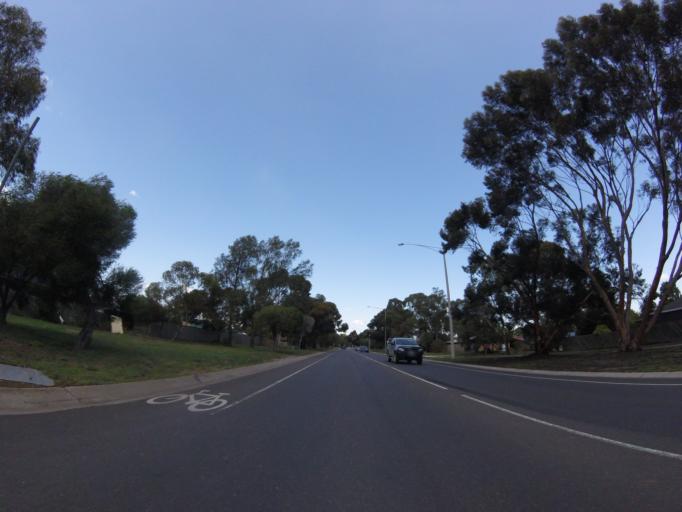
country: AU
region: Victoria
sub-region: Hume
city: Sunbury
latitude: -37.5802
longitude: 144.7492
